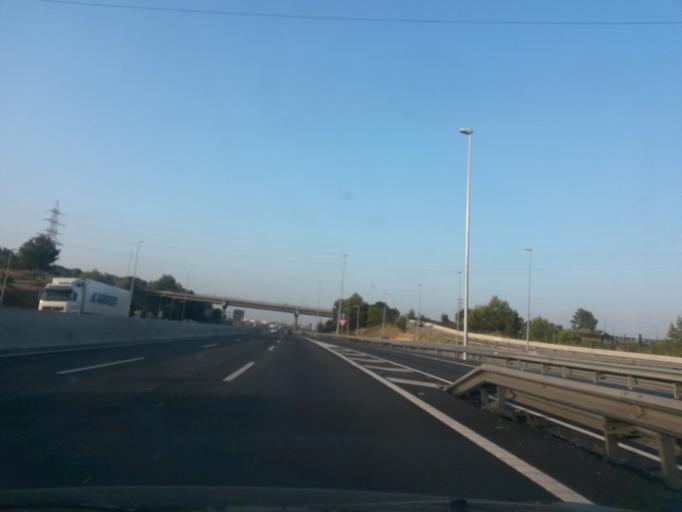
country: ES
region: Catalonia
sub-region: Provincia de Barcelona
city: Barbera del Valles
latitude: 41.4972
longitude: 2.1138
